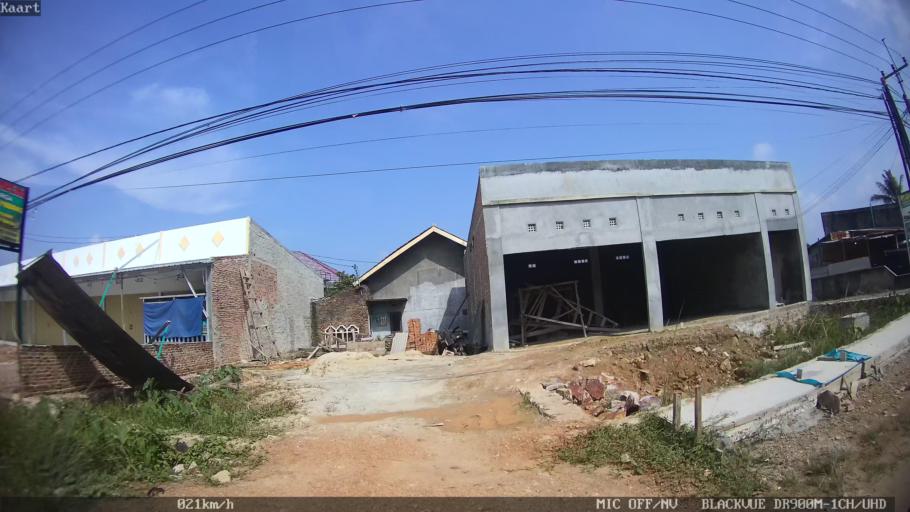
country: ID
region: Lampung
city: Kedaton
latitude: -5.3478
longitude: 105.2664
